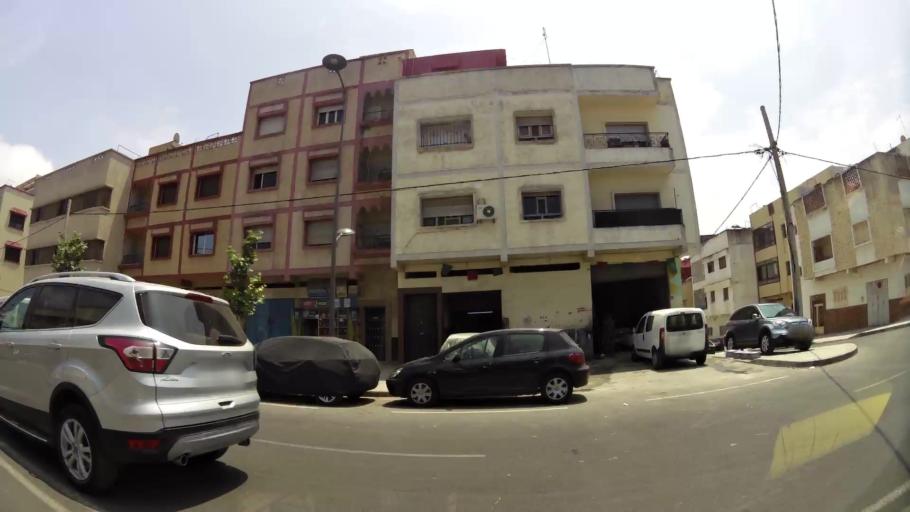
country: MA
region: Rabat-Sale-Zemmour-Zaer
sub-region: Skhirate-Temara
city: Temara
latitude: 33.9805
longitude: -6.8881
